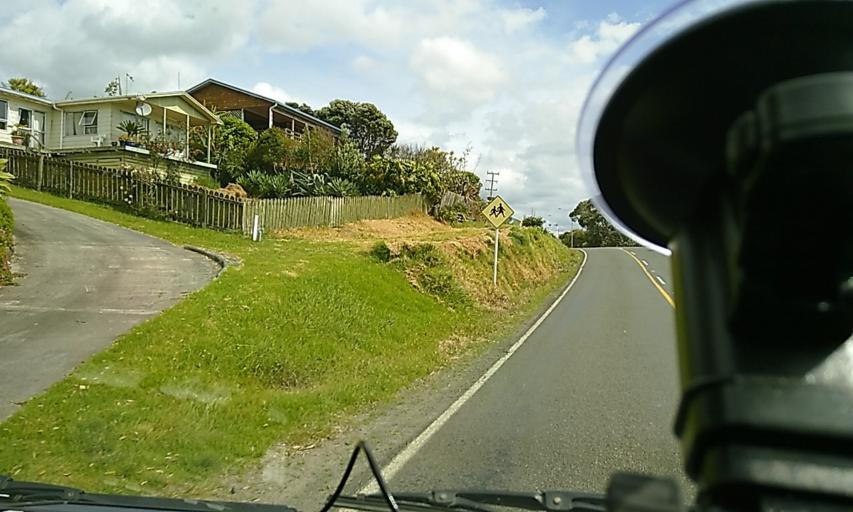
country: NZ
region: Northland
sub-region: Far North District
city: Ahipara
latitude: -35.5121
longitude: 173.3891
